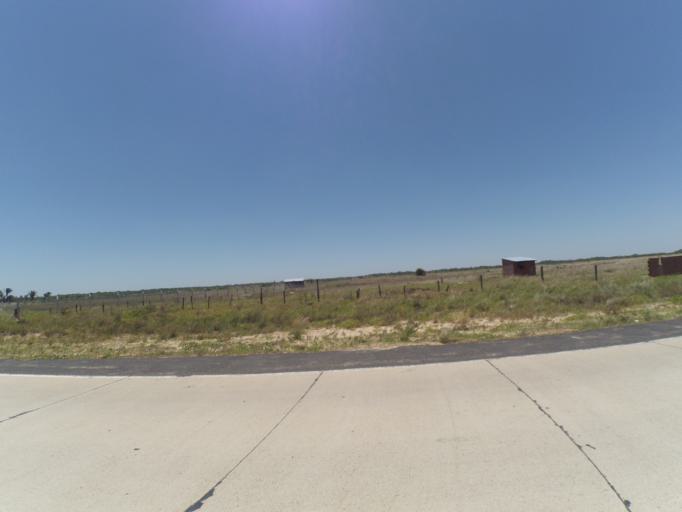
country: BO
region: Santa Cruz
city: Santa Cruz de la Sierra
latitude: -17.7981
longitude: -63.2756
